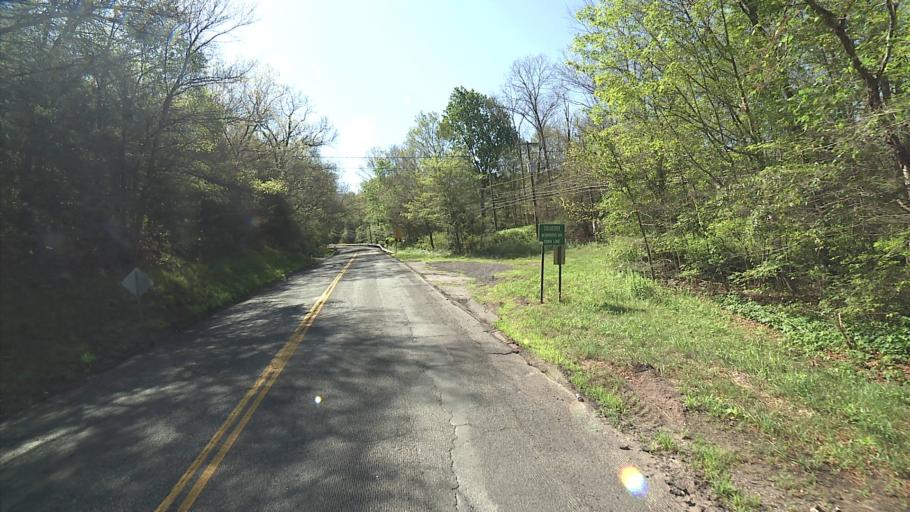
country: US
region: Connecticut
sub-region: Middlesex County
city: Moodus
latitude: 41.5504
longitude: -72.4463
